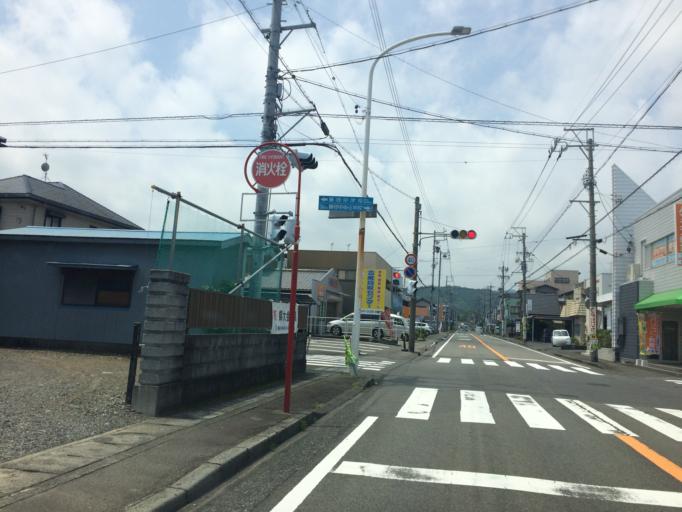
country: JP
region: Shizuoka
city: Fujieda
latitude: 34.8728
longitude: 138.2417
